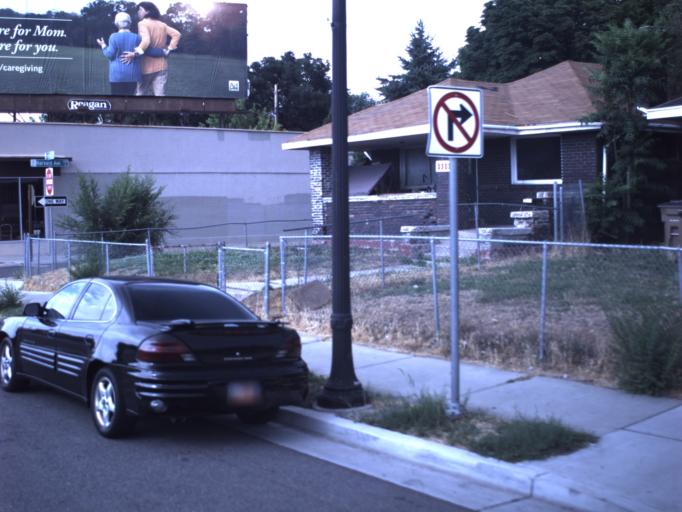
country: US
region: Utah
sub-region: Salt Lake County
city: Salt Lake City
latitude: 40.7446
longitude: -111.8881
